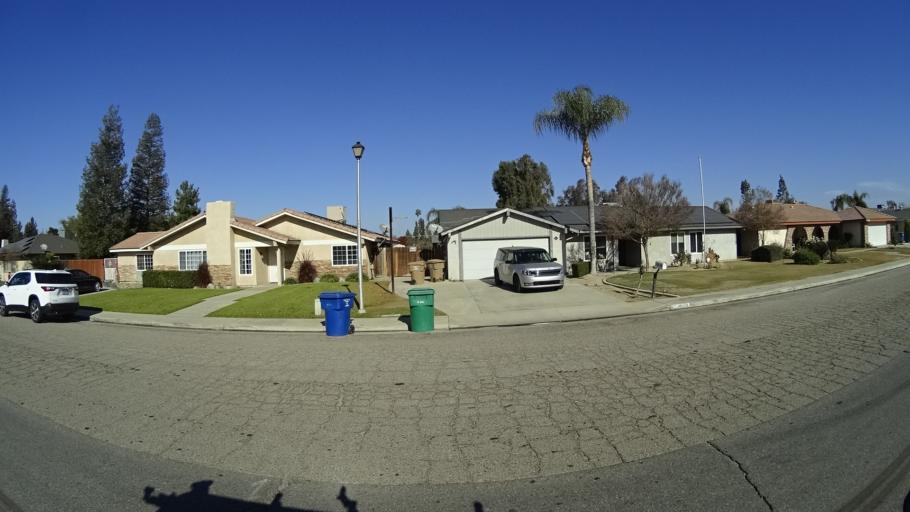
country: US
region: California
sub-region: Kern County
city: Greenacres
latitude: 35.3762
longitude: -119.1253
